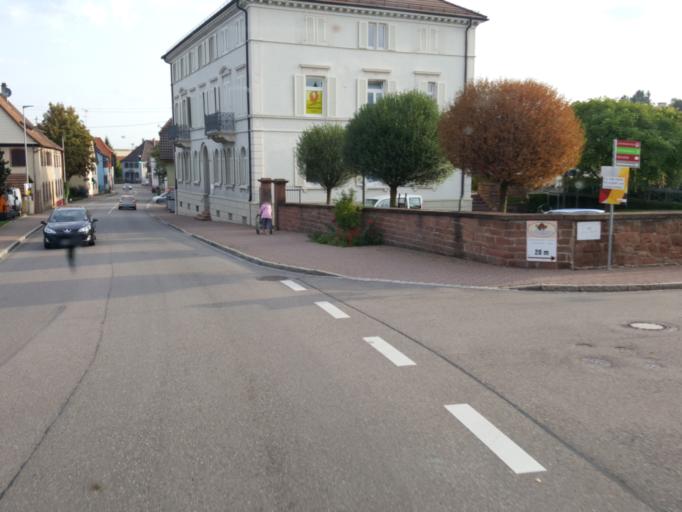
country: DE
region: Baden-Wuerttemberg
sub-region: Freiburg Region
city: Kippenheim
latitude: 48.2918
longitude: 7.8232
